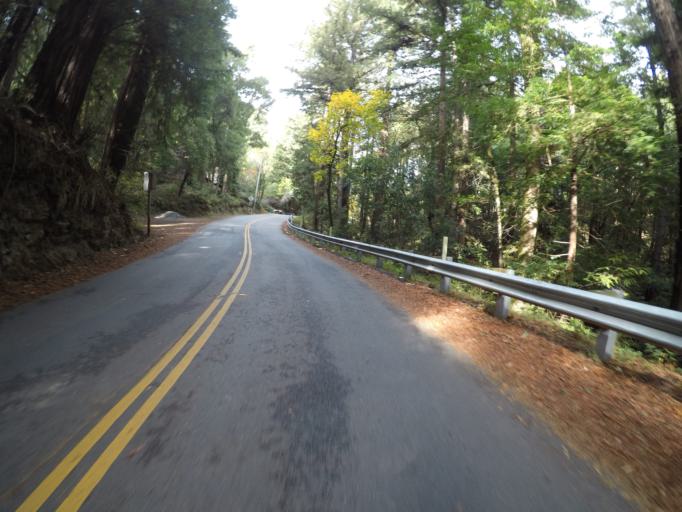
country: US
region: California
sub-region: Santa Cruz County
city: Scotts Valley
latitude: 37.0511
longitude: -121.9975
